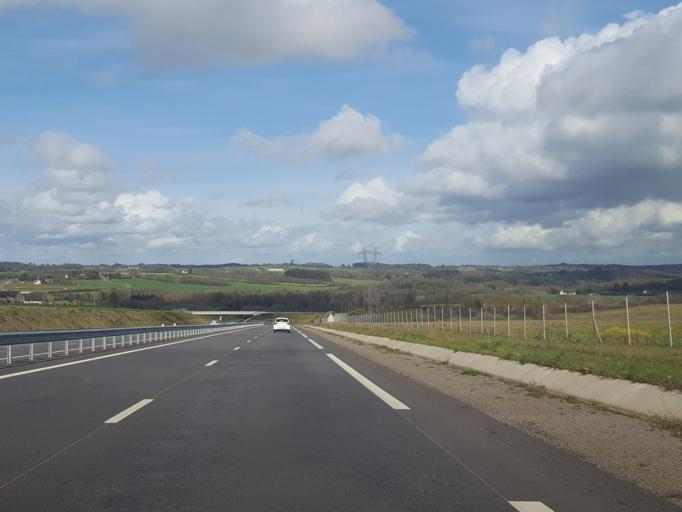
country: FR
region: Brittany
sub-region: Departement d'Ille-et-Vilaine
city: Guignen
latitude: 47.9338
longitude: -1.8375
